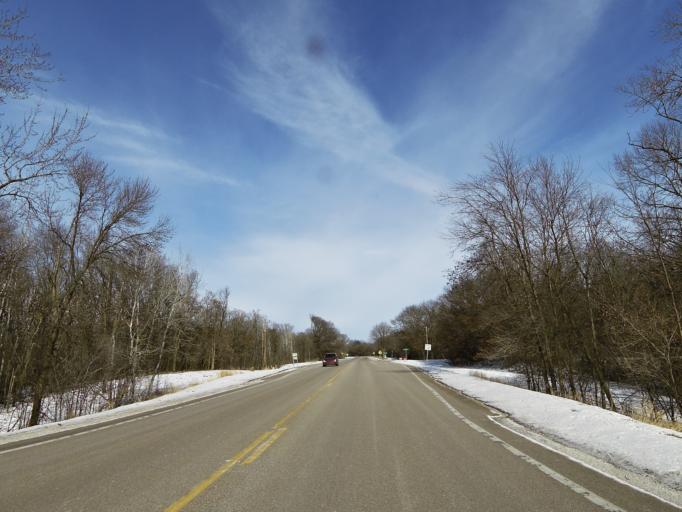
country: US
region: Minnesota
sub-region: Washington County
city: Lake Saint Croix Beach
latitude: 44.9144
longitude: -92.7776
